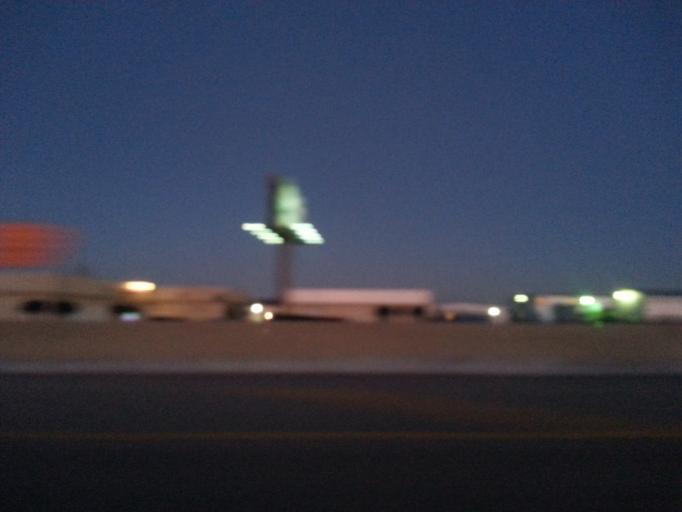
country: US
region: Indiana
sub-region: Lake County
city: Merrillville
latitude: 41.4565
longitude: -87.3221
